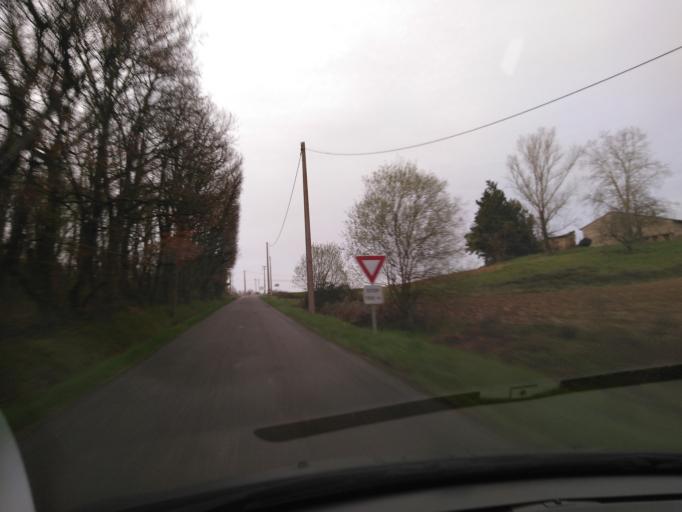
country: FR
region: Midi-Pyrenees
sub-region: Departement du Tarn-et-Garonne
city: Verdun-sur-Garonne
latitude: 43.8530
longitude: 1.1392
